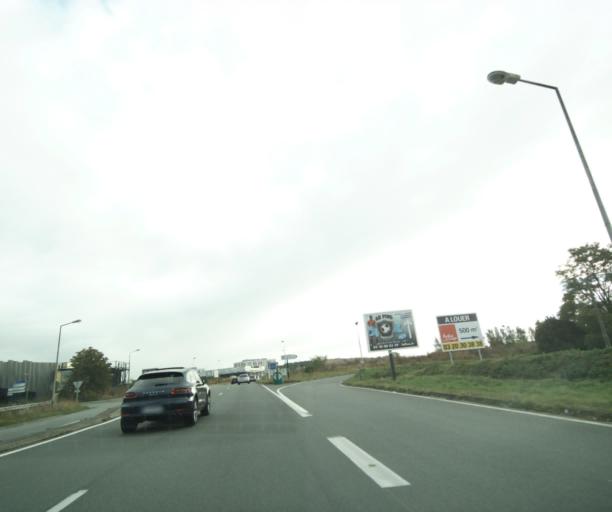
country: FR
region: Nord-Pas-de-Calais
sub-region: Departement du Nord
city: Vendeville
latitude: 50.5817
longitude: 3.0932
